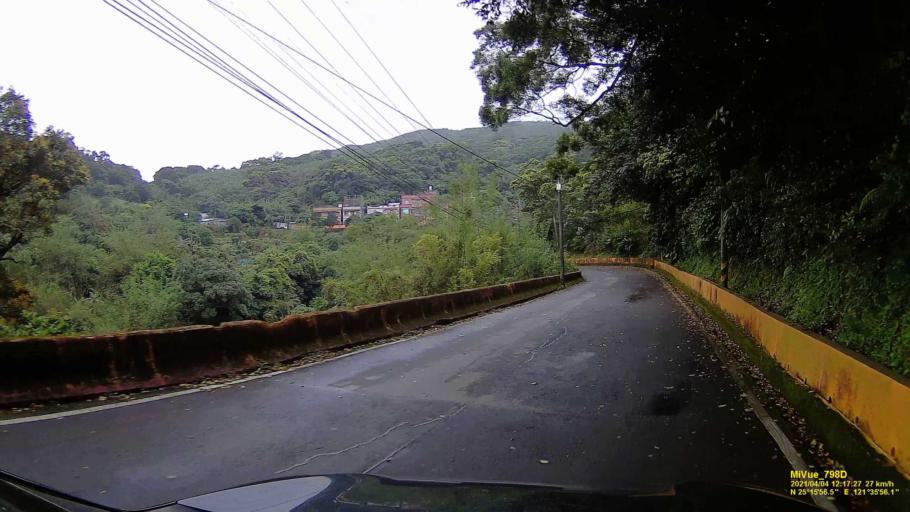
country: TW
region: Taiwan
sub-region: Keelung
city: Keelung
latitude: 25.2658
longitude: 121.5988
